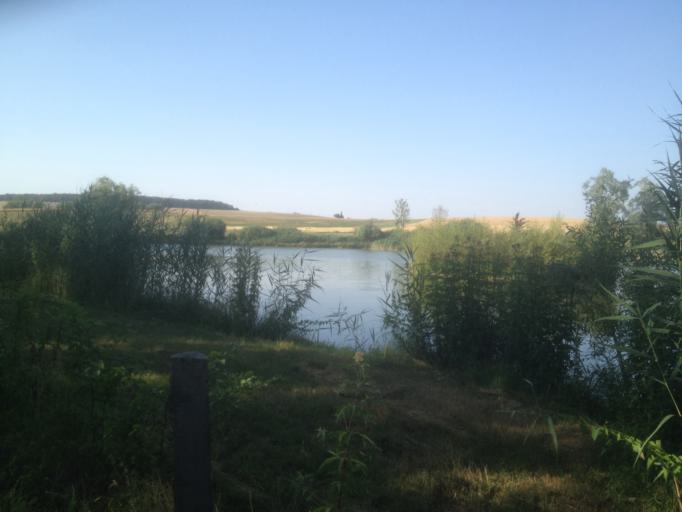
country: FR
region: Champagne-Ardenne
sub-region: Departement de la Haute-Marne
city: Joinville
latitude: 48.4573
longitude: 5.3268
